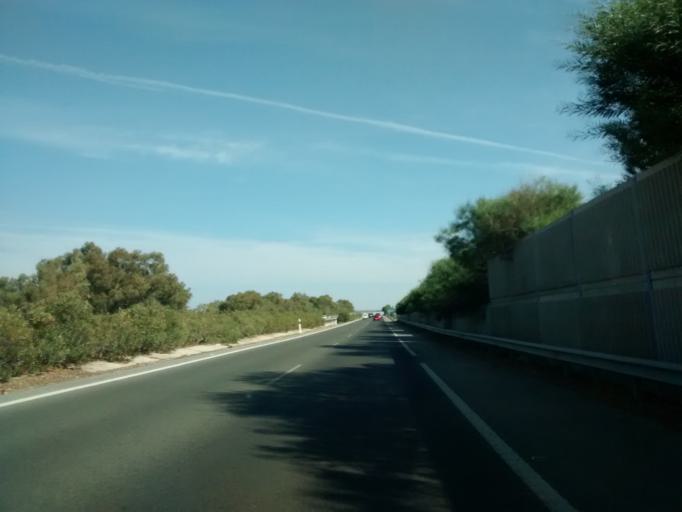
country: ES
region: Andalusia
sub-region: Provincia de Cadiz
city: Chiclana de la Frontera
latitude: 36.3728
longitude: -6.1132
